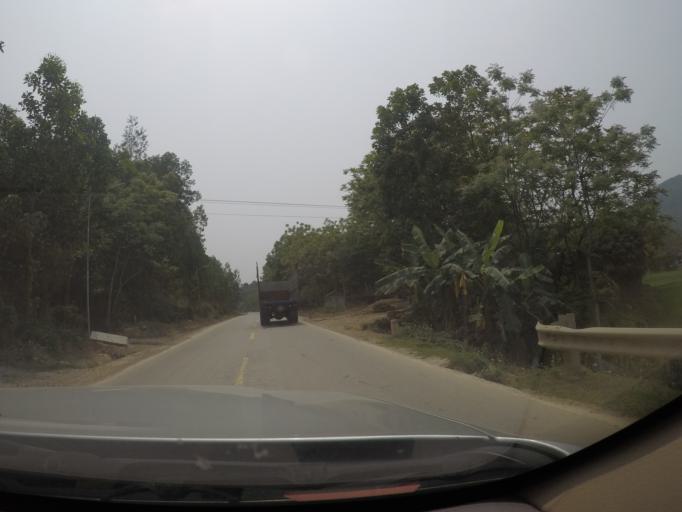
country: VN
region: Thanh Hoa
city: Thi Tran Yen Cat
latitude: 19.7307
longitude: 105.4261
